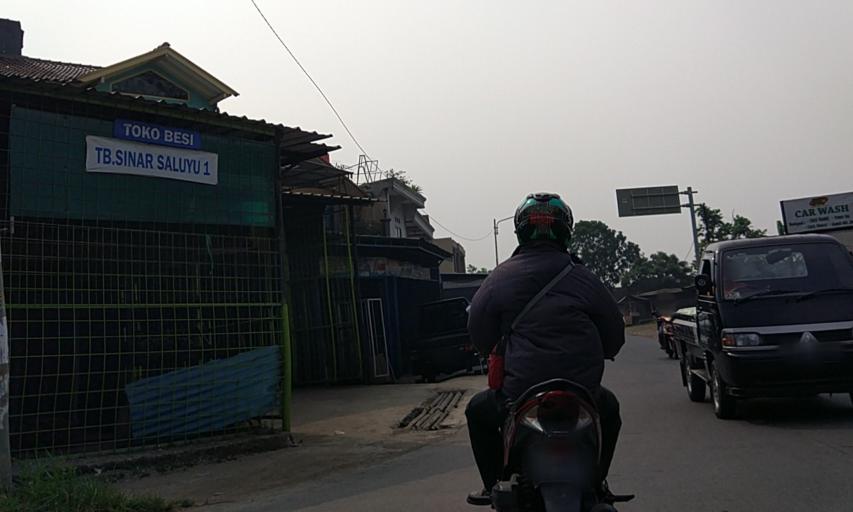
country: ID
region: West Java
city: Soreang
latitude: -7.0398
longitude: 107.5518
